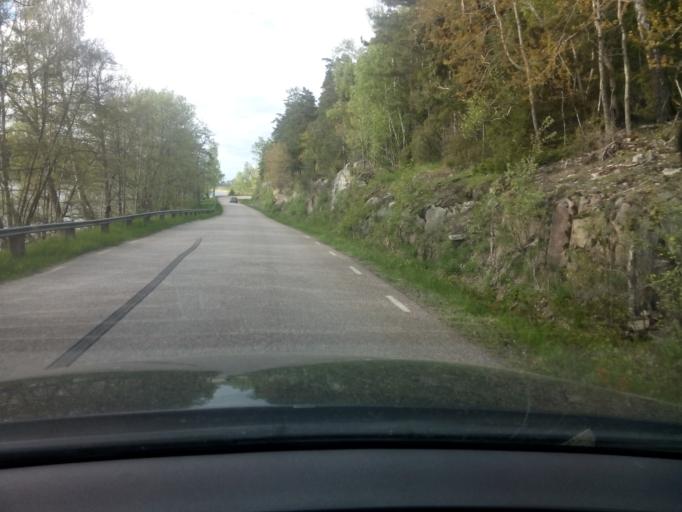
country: SE
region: Soedermanland
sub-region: Nykopings Kommun
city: Stigtomta
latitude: 58.9387
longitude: 16.8909
